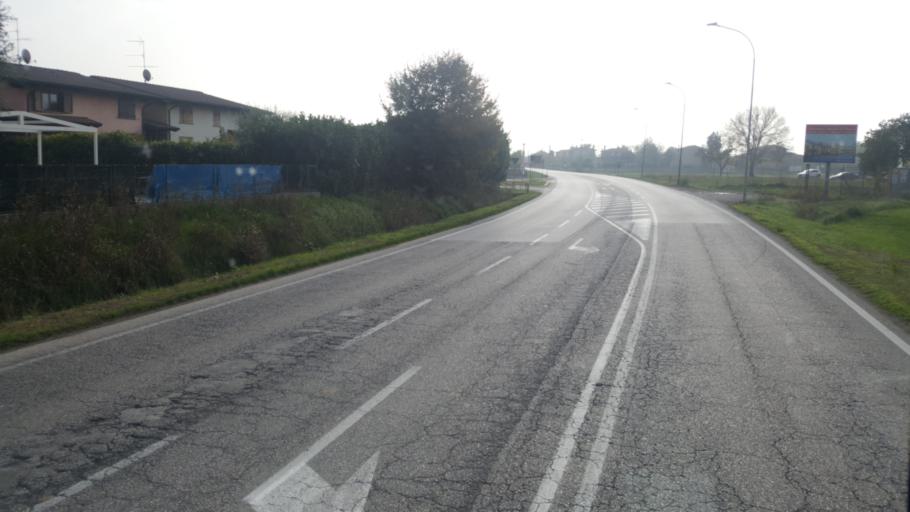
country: IT
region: Lombardy
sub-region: Provincia di Mantova
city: Castellucchio
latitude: 45.1810
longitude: 10.6698
